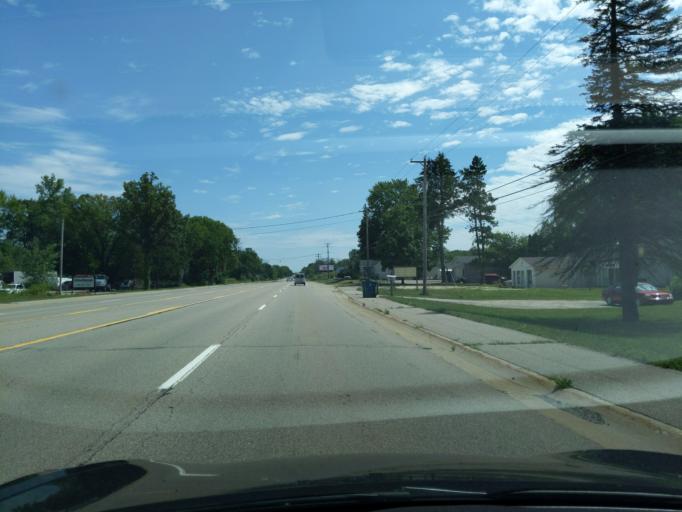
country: US
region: Michigan
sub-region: Midland County
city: Midland
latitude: 43.6123
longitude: -84.3527
